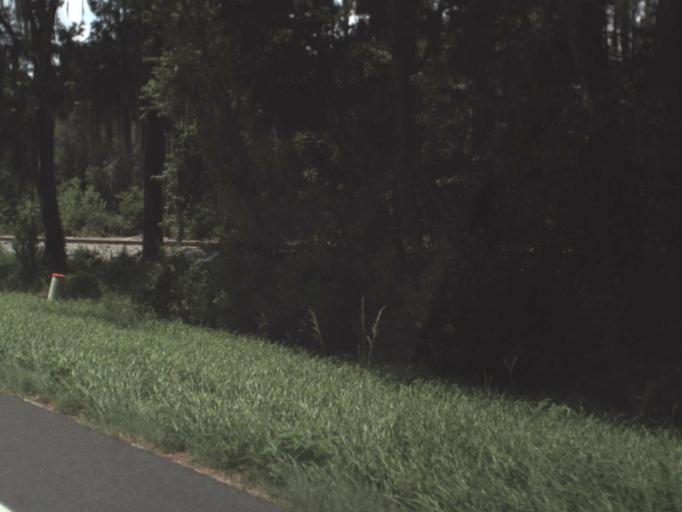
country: US
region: Florida
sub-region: Suwannee County
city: Wellborn
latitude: 30.3822
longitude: -82.8150
